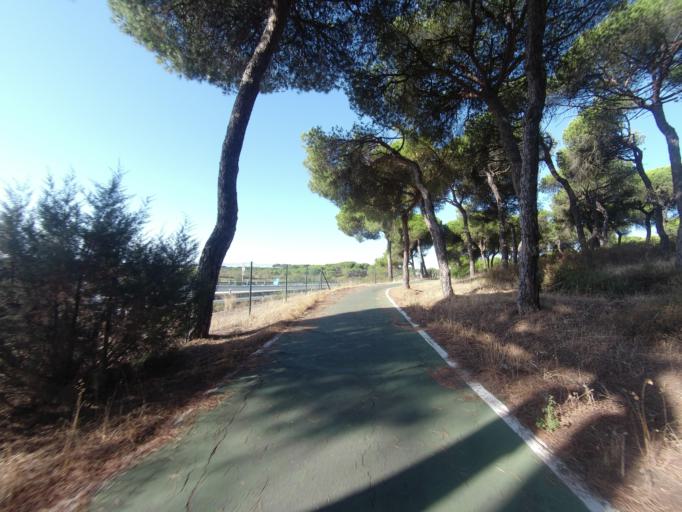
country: ES
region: Andalusia
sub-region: Provincia de Huelva
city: Aljaraque
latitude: 37.2175
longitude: -7.0246
